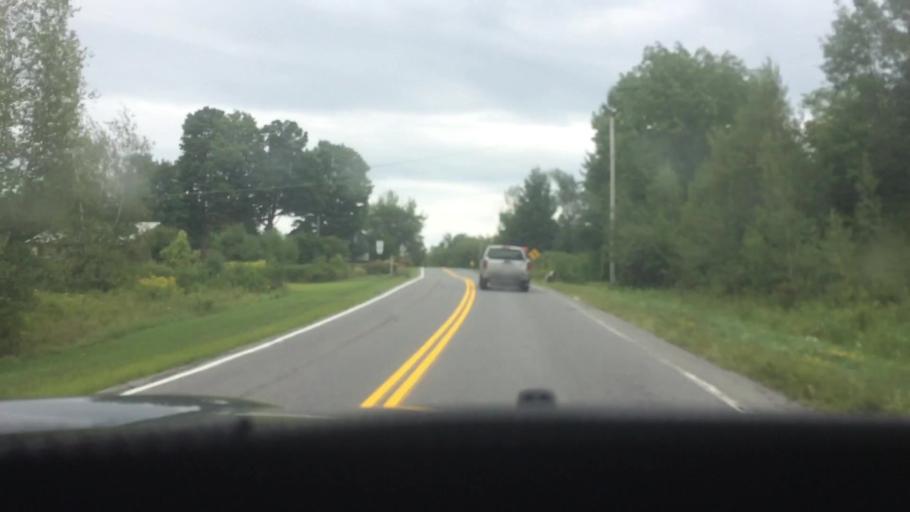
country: US
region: New York
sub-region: St. Lawrence County
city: Canton
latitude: 44.5353
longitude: -75.1733
